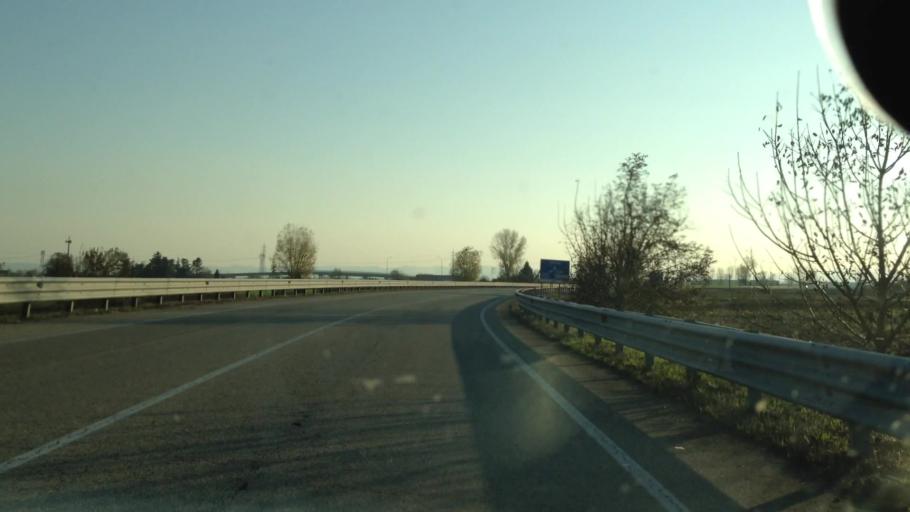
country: IT
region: Piedmont
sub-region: Provincia di Vercelli
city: Cigliano
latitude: 45.3021
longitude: 8.0407
